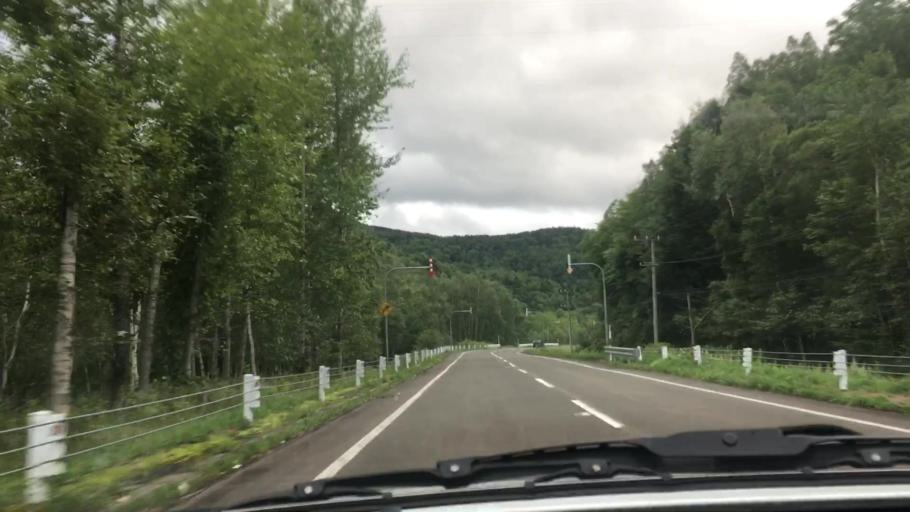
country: JP
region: Hokkaido
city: Shimo-furano
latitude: 43.0522
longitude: 142.5331
